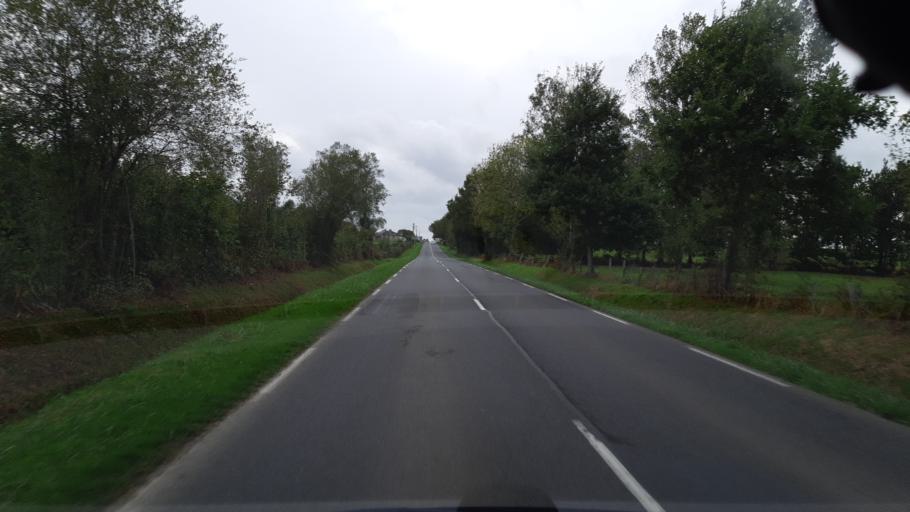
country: FR
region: Lower Normandy
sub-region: Departement de la Manche
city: Gavray
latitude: 48.9350
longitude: -1.3725
